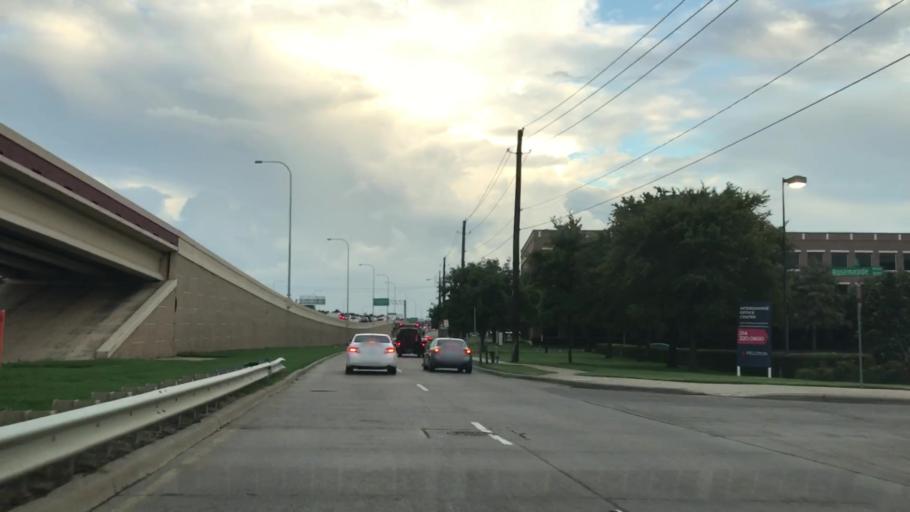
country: US
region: Texas
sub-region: Dallas County
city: Addison
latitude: 33.0100
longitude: -96.8297
